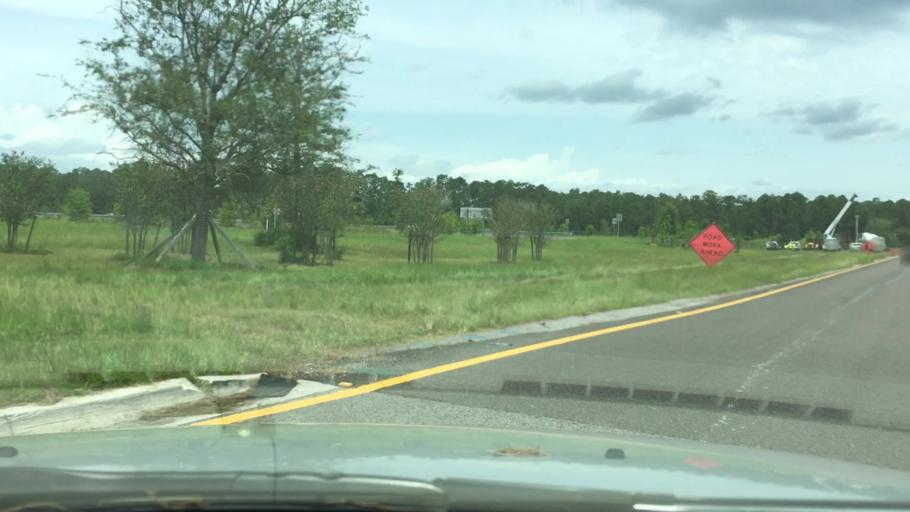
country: US
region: Florida
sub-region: Volusia County
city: Lake Helen
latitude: 29.0180
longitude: -81.2279
